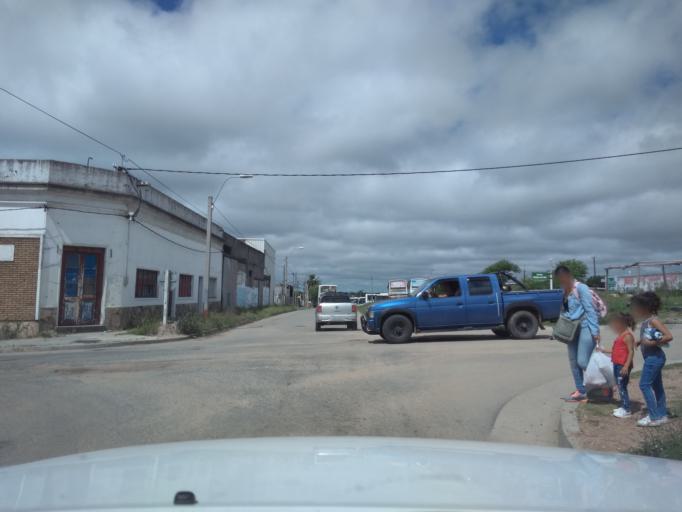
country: UY
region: Canelones
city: Pando
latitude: -34.7155
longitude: -55.9626
